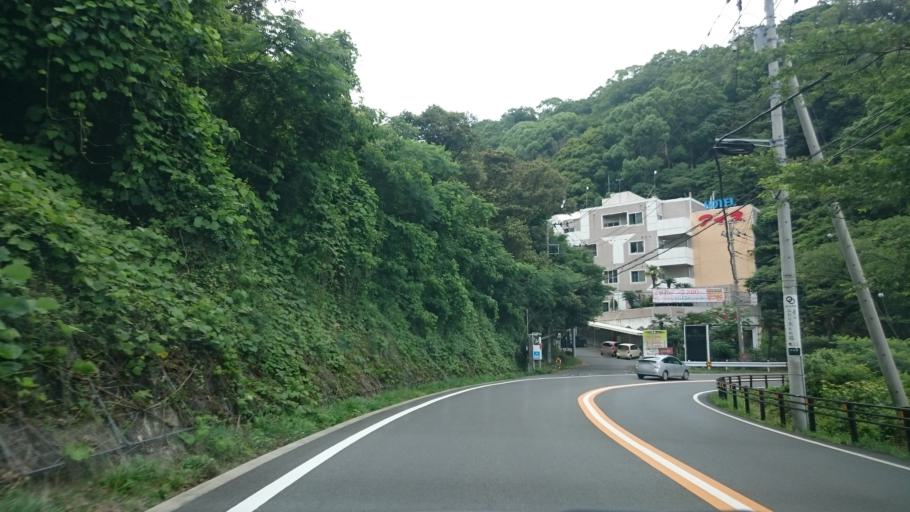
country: JP
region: Shizuoka
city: Atami
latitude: 35.0306
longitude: 139.0959
